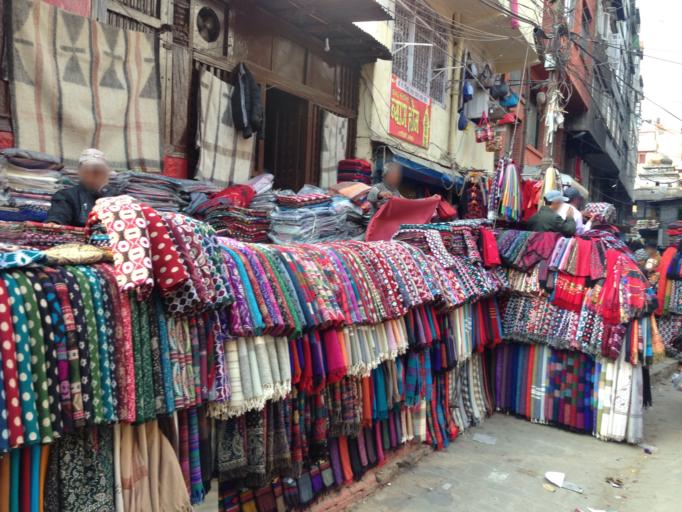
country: NP
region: Central Region
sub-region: Bagmati Zone
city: Kathmandu
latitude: 27.7062
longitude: 85.3097
